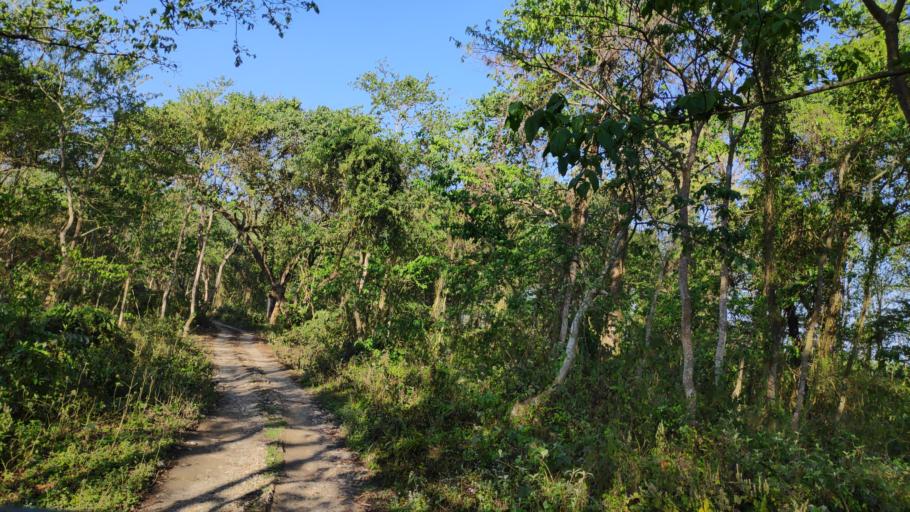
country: NP
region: Central Region
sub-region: Narayani Zone
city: Bharatpur
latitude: 27.5594
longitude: 84.5615
